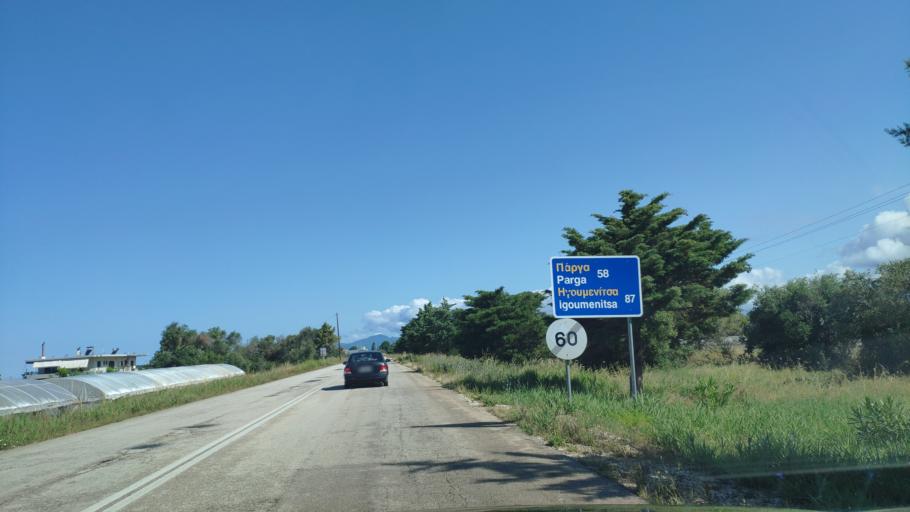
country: GR
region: Epirus
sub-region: Nomos Prevezis
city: Preveza
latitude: 38.9769
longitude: 20.7189
